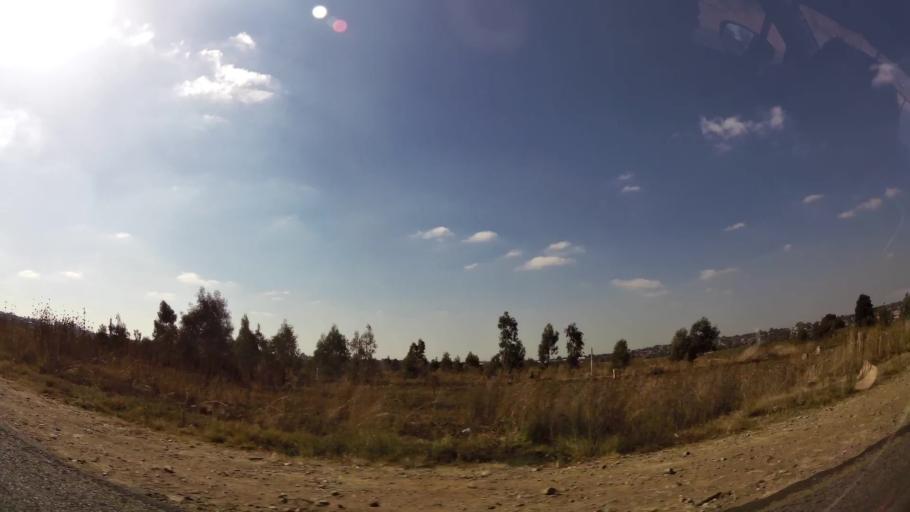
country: ZA
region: Gauteng
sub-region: City of Johannesburg Metropolitan Municipality
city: Roodepoort
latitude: -26.1336
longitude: 27.8176
